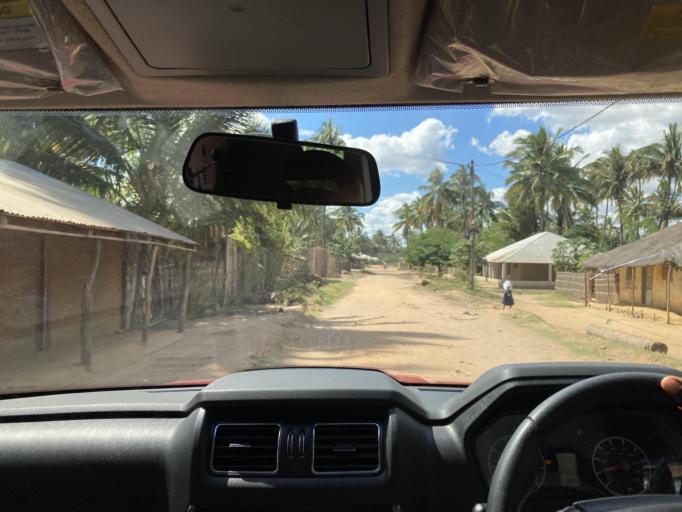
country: MZ
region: Cabo Delgado
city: Montepuez
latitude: -13.1385
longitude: 39.0008
